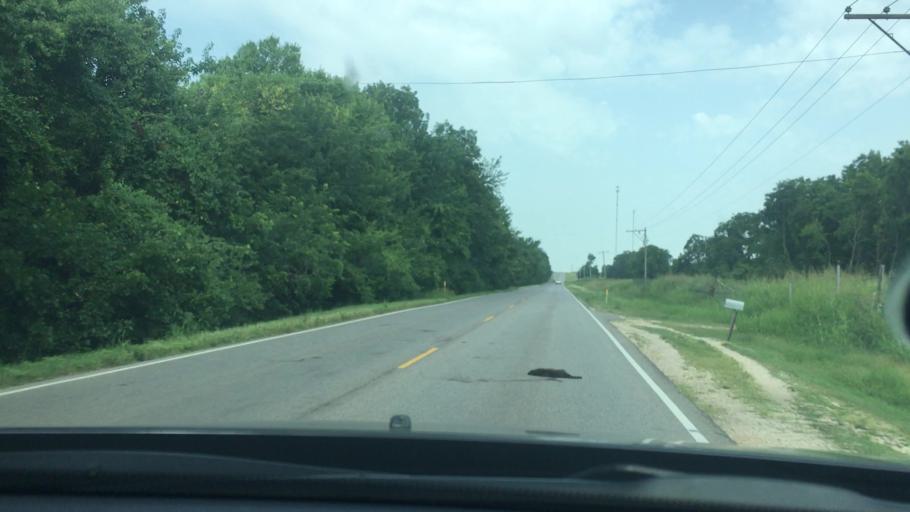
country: US
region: Oklahoma
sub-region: Garvin County
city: Stratford
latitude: 34.7968
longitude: -96.8698
